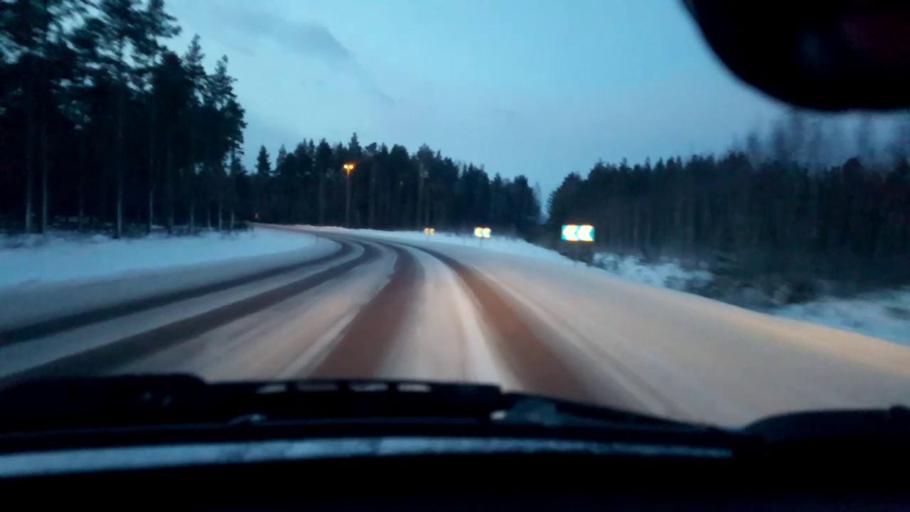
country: SE
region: Dalarna
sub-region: Mora Kommun
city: Mora
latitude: 60.9570
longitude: 14.5331
